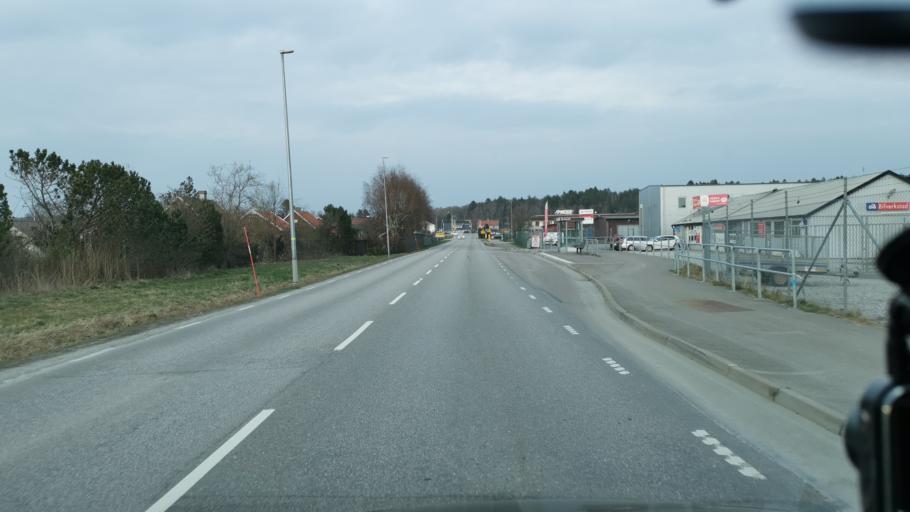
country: SE
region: Vaestra Goetaland
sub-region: Kungalvs Kommun
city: Kode
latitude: 57.9398
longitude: 11.8497
